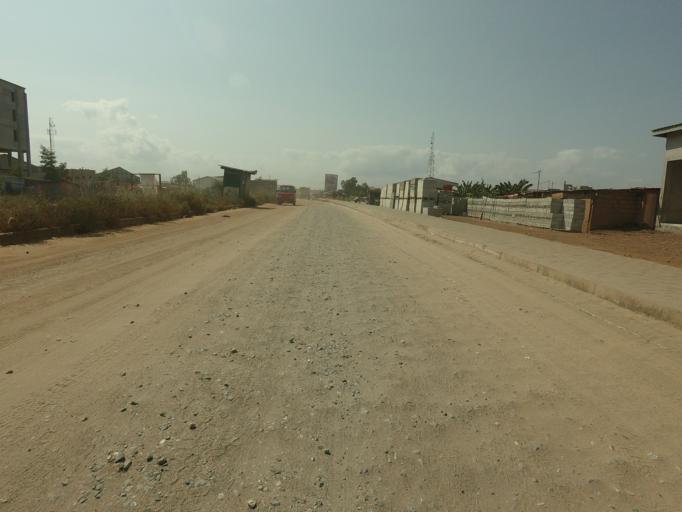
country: GH
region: Greater Accra
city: Medina Estates
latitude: 5.6349
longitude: -0.1252
